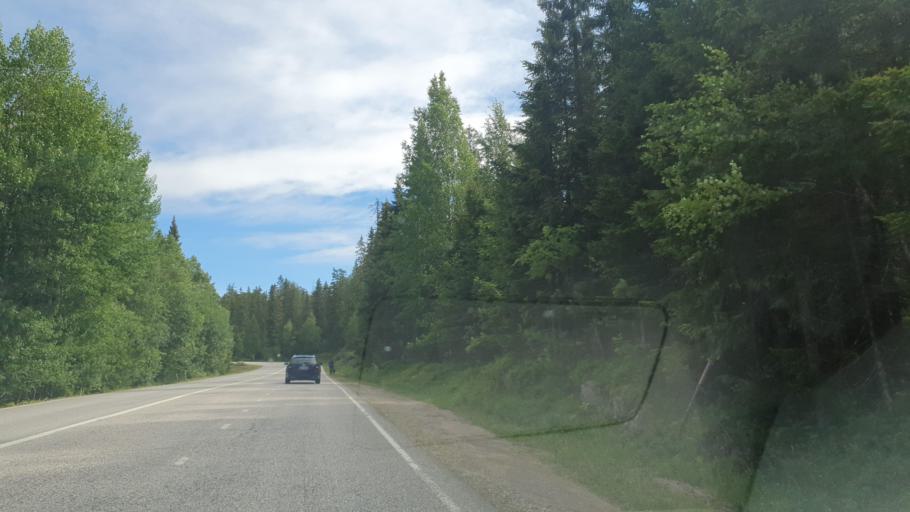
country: FI
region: Kainuu
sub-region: Kajaani
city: Vuokatti
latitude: 64.1294
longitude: 28.2551
